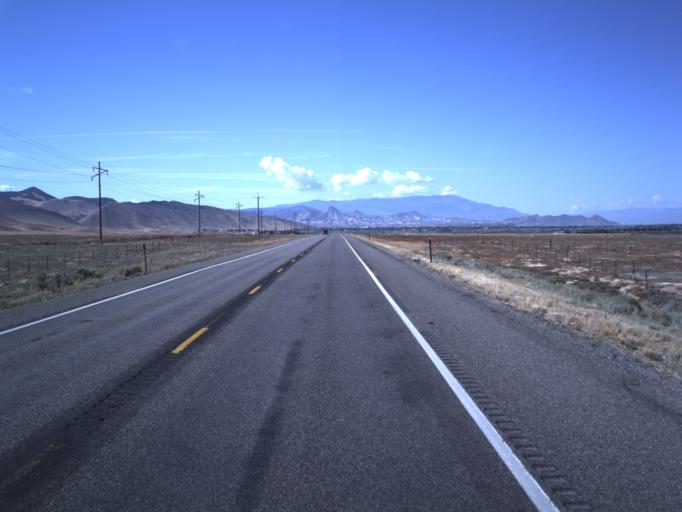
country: US
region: Utah
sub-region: Sevier County
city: Salina
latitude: 39.0311
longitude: -111.8296
